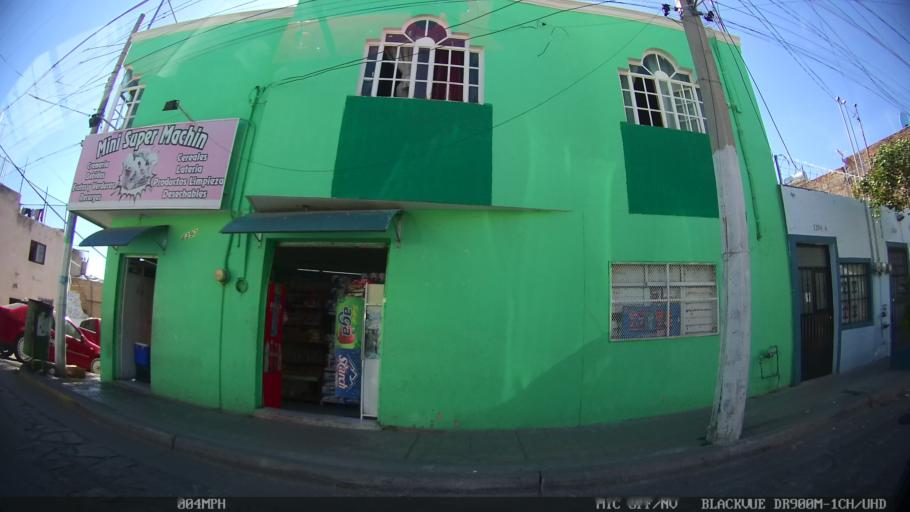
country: MX
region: Jalisco
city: Tlaquepaque
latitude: 20.6814
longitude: -103.2680
